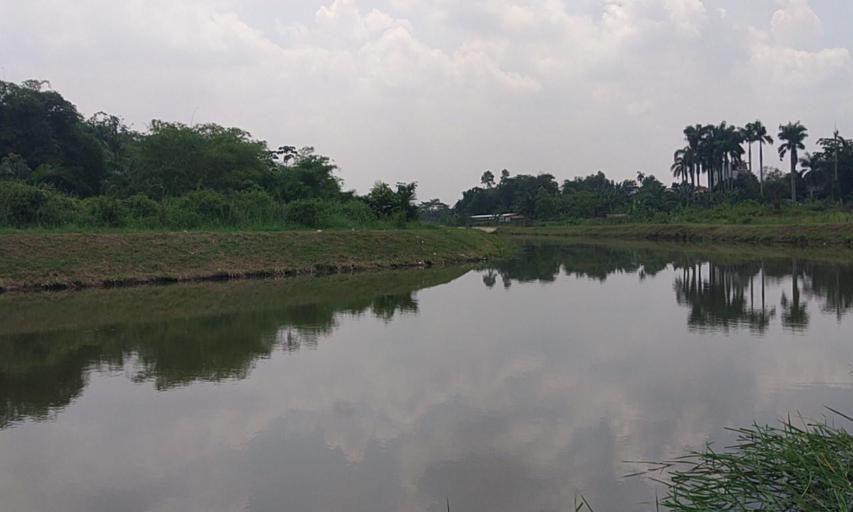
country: ID
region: West Java
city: Parung
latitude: -6.4761
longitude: 106.7751
